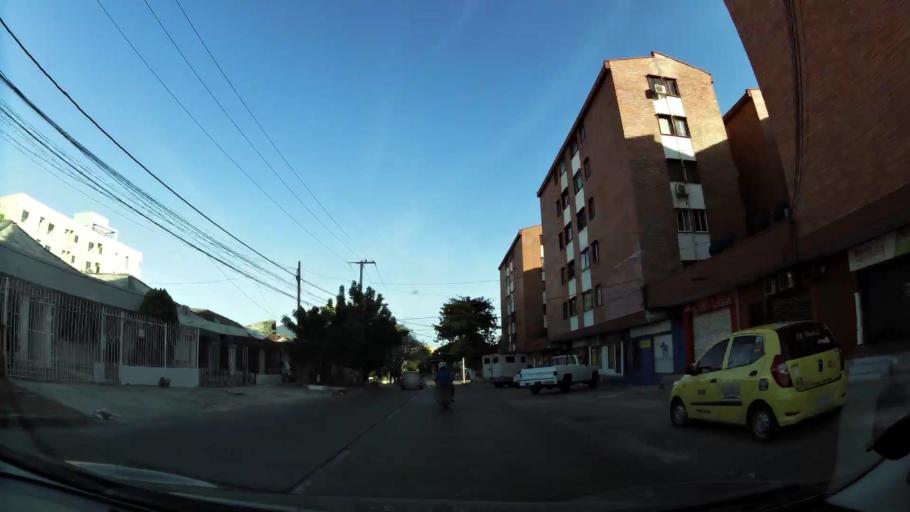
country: CO
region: Atlantico
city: Barranquilla
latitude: 10.9872
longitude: -74.8046
